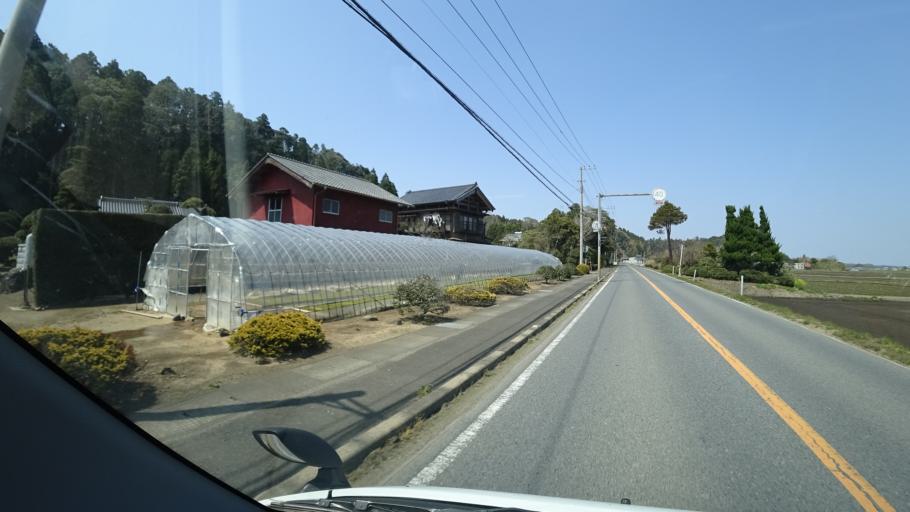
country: JP
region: Chiba
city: Yokaichiba
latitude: 35.6796
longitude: 140.4652
